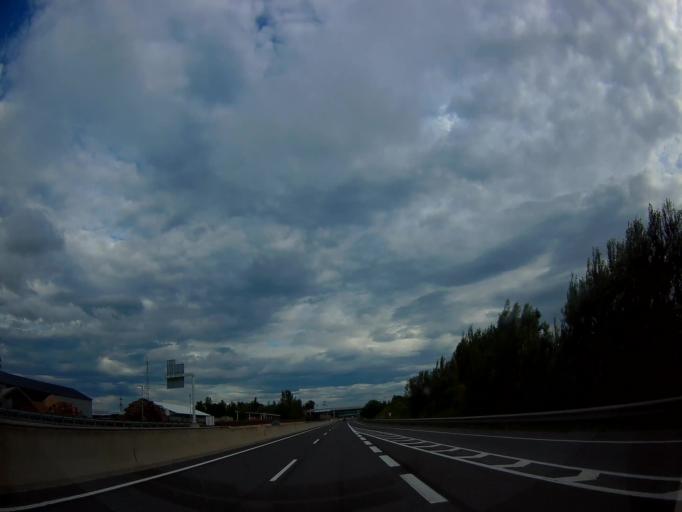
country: AT
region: Lower Austria
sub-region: Politischer Bezirk Sankt Polten
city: Traismauer
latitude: 48.3677
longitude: 15.7175
